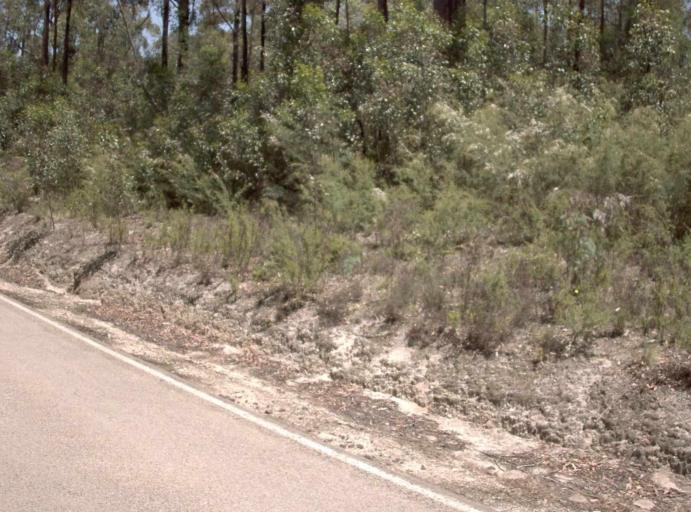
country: AU
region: Victoria
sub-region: East Gippsland
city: Lakes Entrance
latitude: -37.6471
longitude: 147.8937
